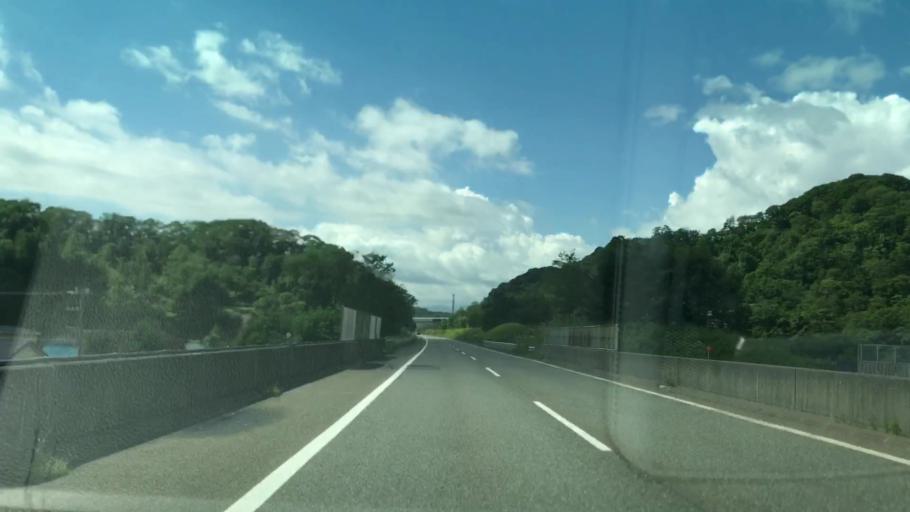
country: JP
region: Hokkaido
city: Shiraoi
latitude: 42.5687
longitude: 141.3423
